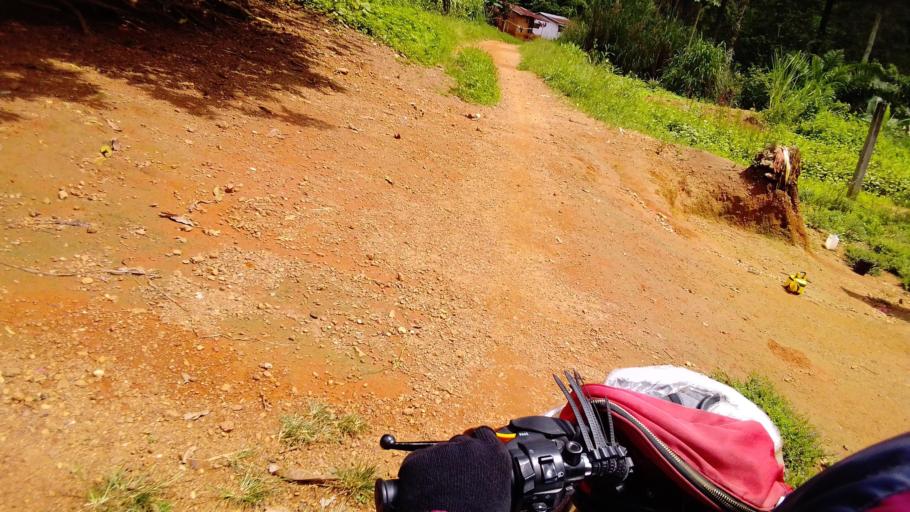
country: SL
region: Eastern Province
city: Koyima
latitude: 8.6783
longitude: -11.0065
